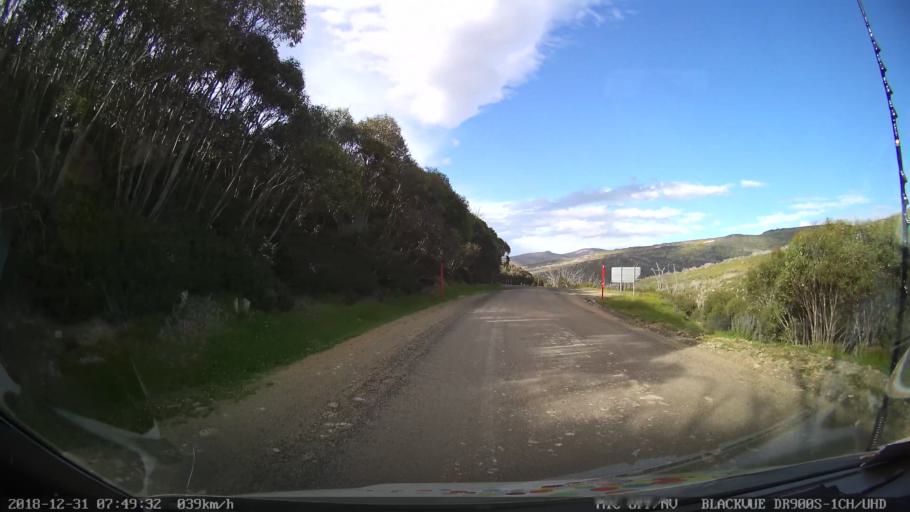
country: AU
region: New South Wales
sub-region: Snowy River
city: Jindabyne
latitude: -36.3718
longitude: 148.3851
